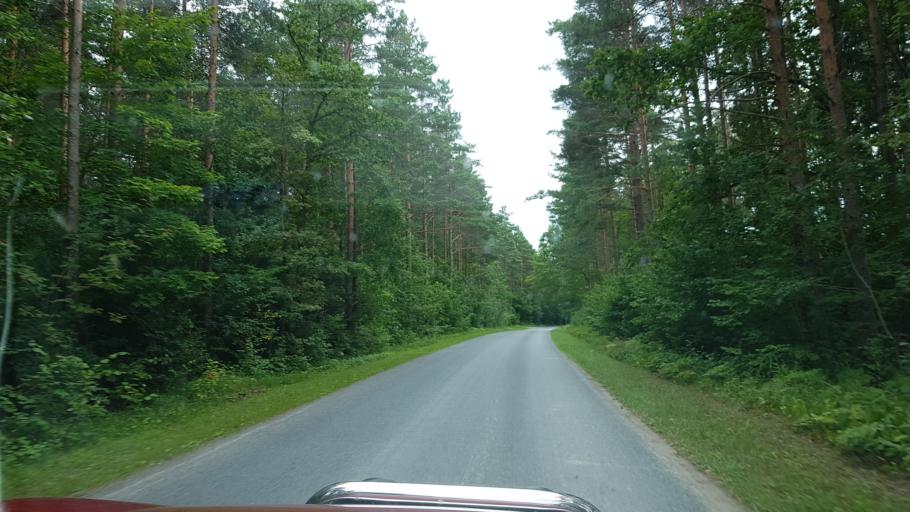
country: EE
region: Laeaene
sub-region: Lihula vald
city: Lihula
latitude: 58.9796
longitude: 23.8899
